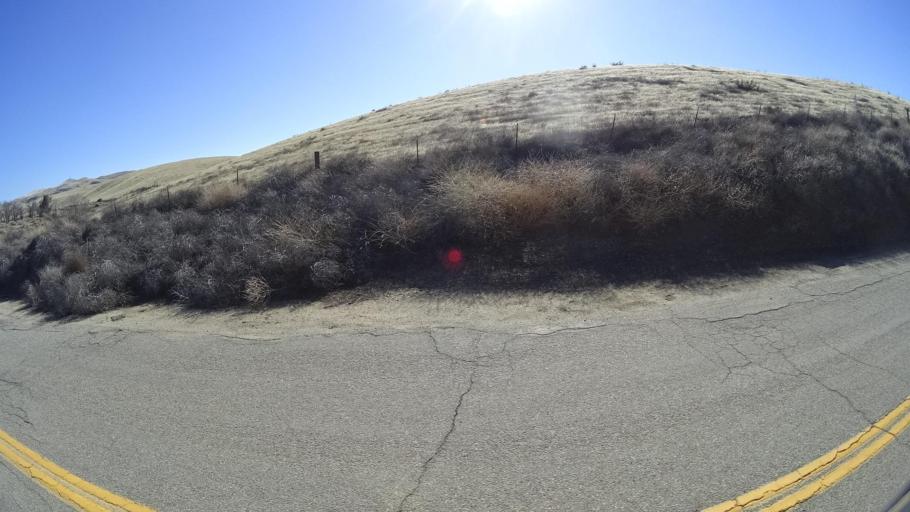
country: US
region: California
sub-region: Kern County
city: Maricopa
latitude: 34.9591
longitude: -119.4436
